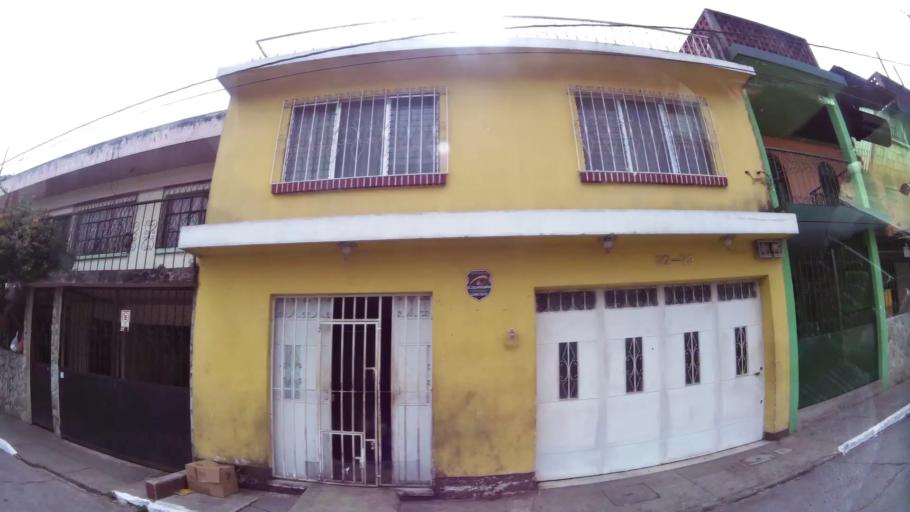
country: GT
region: Guatemala
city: Guatemala City
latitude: 14.6400
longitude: -90.5552
